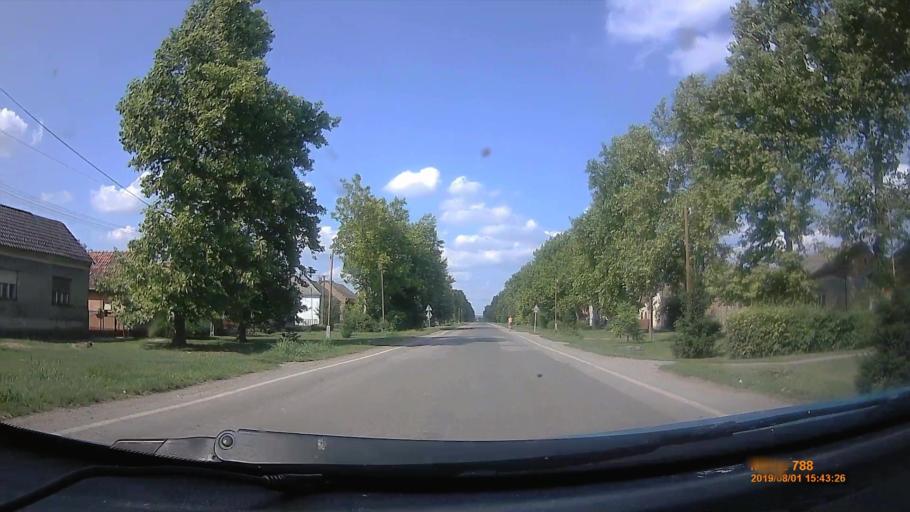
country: HU
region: Baranya
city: Szentlorinc
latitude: 45.9996
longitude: 17.9696
